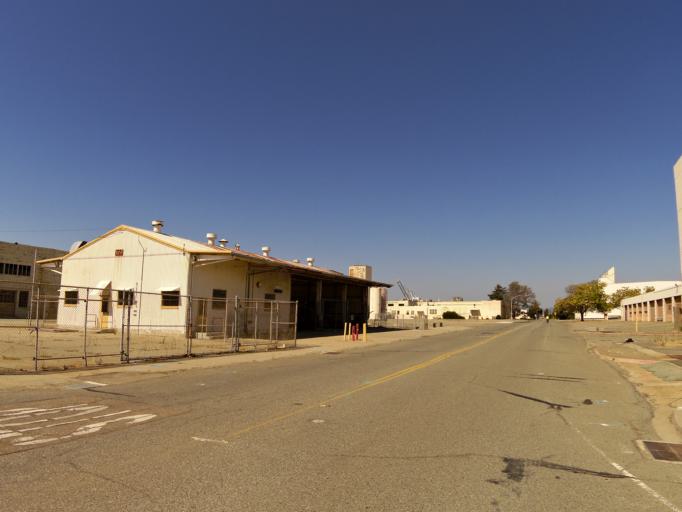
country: US
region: California
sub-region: Alameda County
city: Oakland
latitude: 37.7834
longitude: -122.3035
